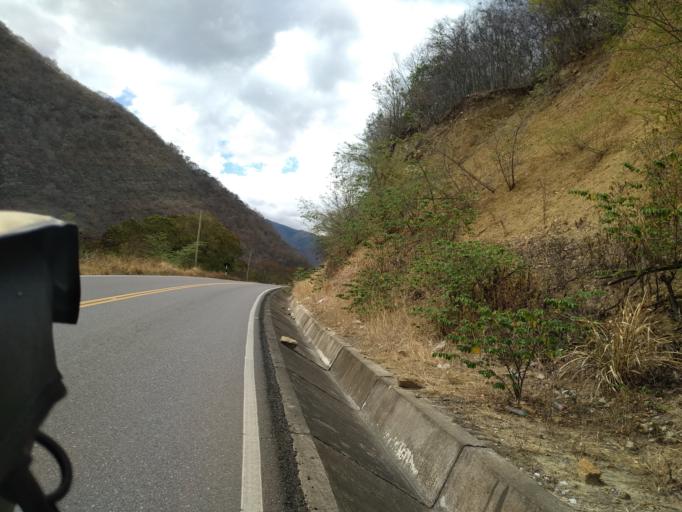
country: PE
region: Amazonas
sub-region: Utcubamba
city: Jamalca
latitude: -5.8700
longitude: -78.2154
